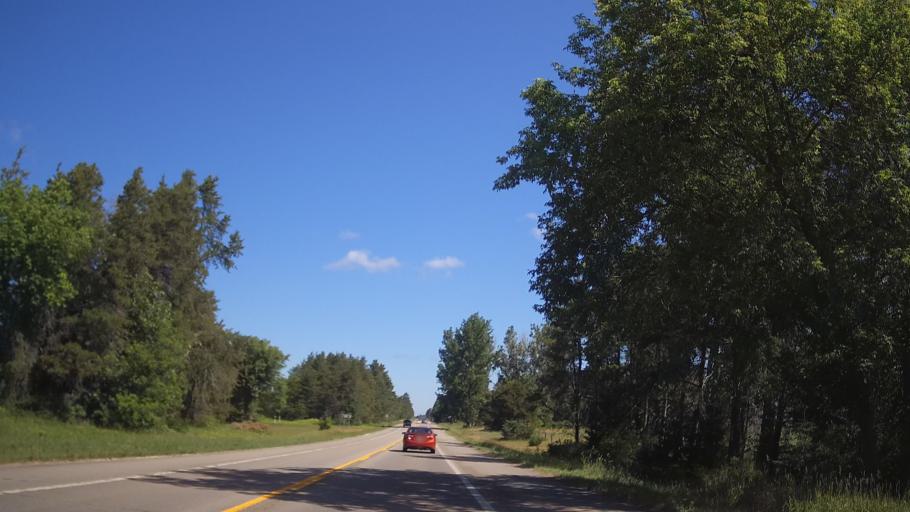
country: US
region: Michigan
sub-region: Cheboygan County
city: Indian River
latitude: 45.4970
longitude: -84.7812
